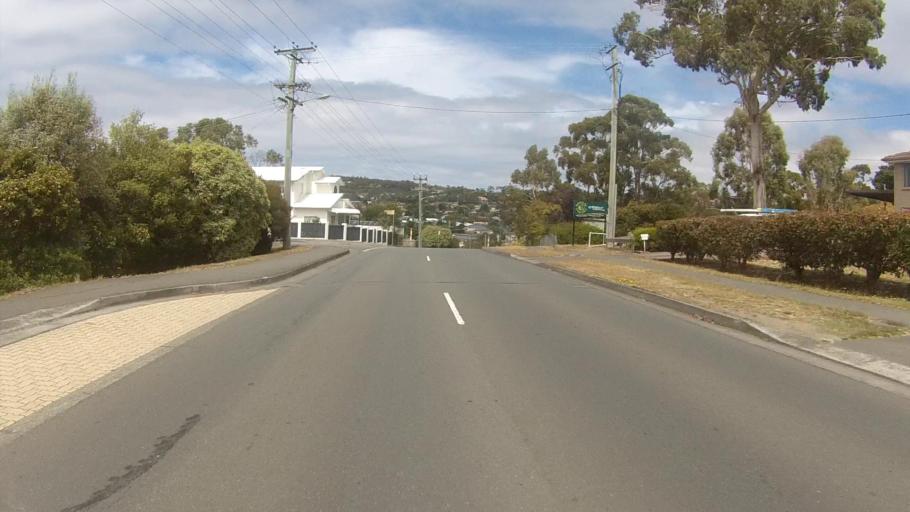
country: AU
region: Tasmania
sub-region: Kingborough
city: Blackmans Bay
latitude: -42.9964
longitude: 147.3231
